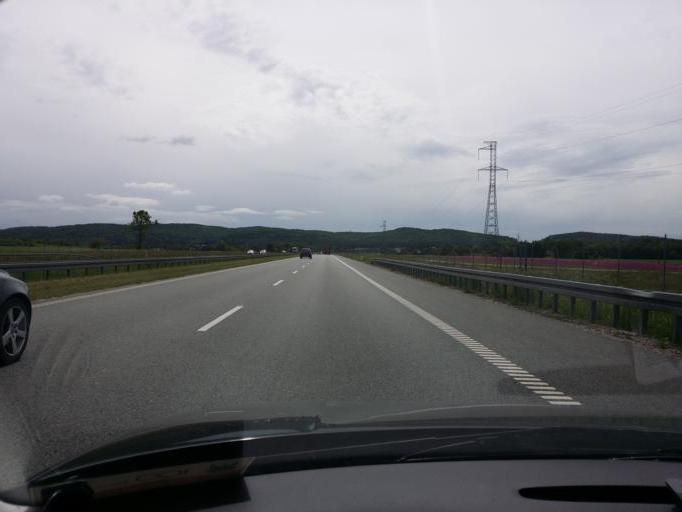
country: PL
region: Swietokrzyskie
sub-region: Powiat kielecki
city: Piekoszow
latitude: 50.8706
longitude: 20.5162
